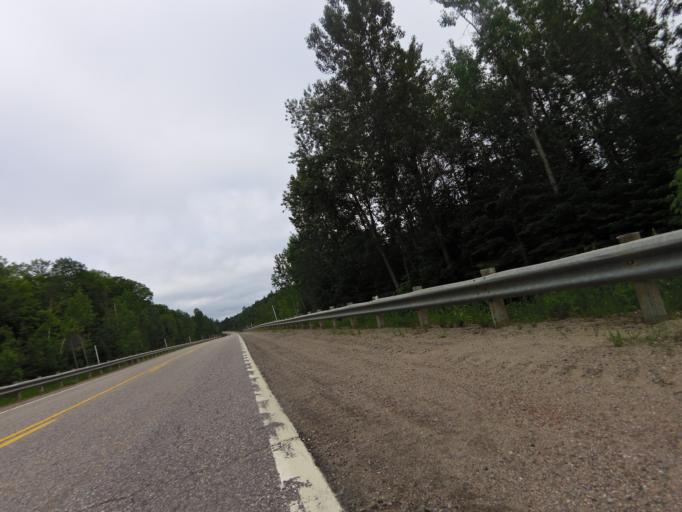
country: CA
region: Quebec
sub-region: Outaouais
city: Shawville
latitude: 45.9133
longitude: -76.3246
